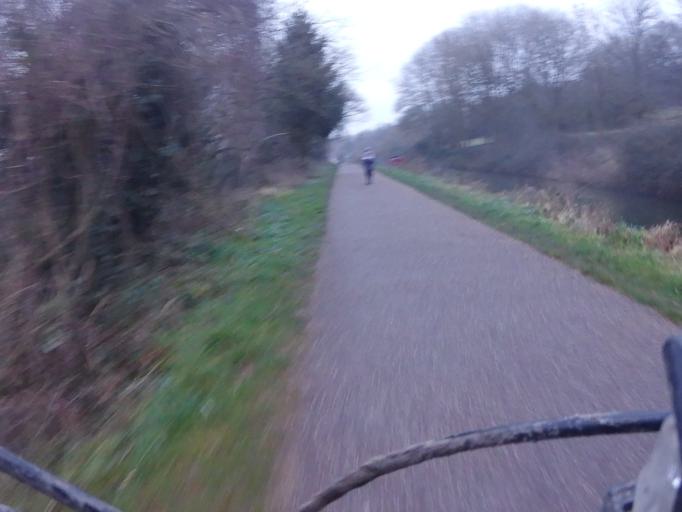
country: GB
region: England
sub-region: Bath and North East Somerset
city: Bath
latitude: 51.3910
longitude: -2.3438
